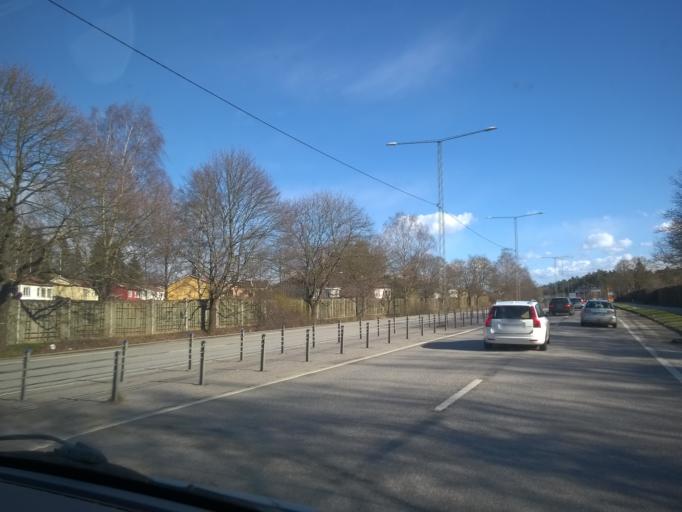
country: SE
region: Stockholm
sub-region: Stockholms Kommun
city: Bromma
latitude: 59.3490
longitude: 17.8899
